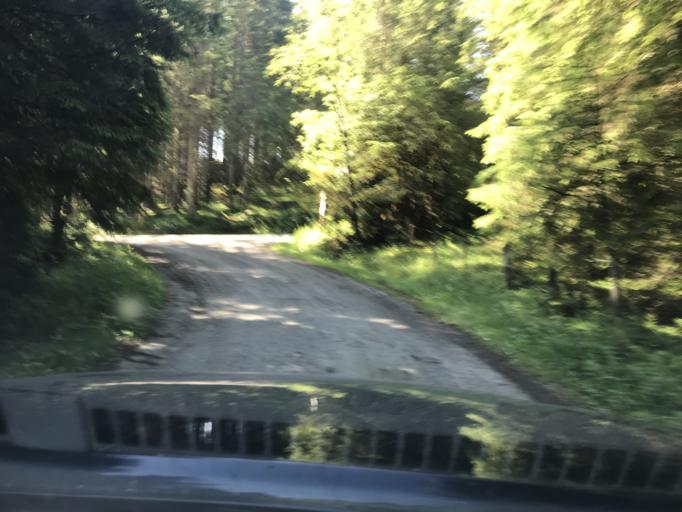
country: AT
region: Styria
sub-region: Politischer Bezirk Murau
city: Sankt Peter am Kammersberg
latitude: 47.2157
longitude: 14.1770
